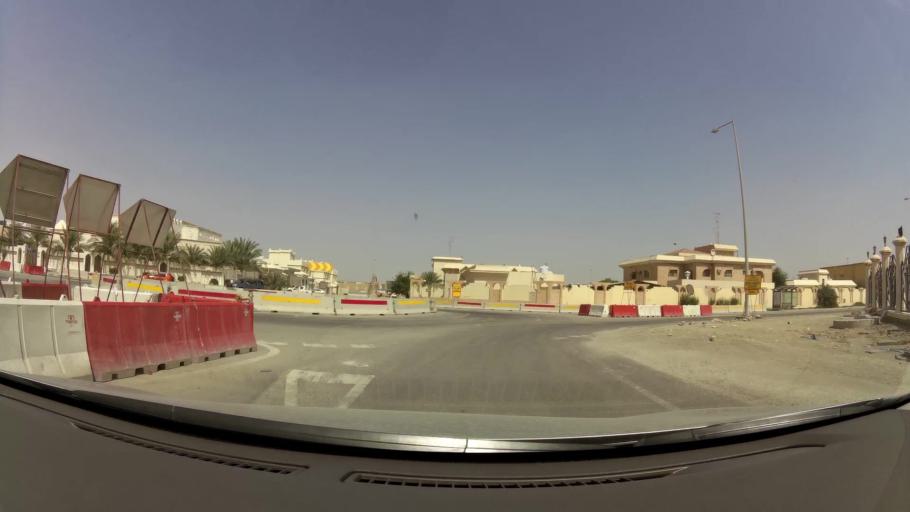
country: QA
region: Baladiyat Umm Salal
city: Umm Salal Muhammad
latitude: 25.3824
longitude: 51.4354
